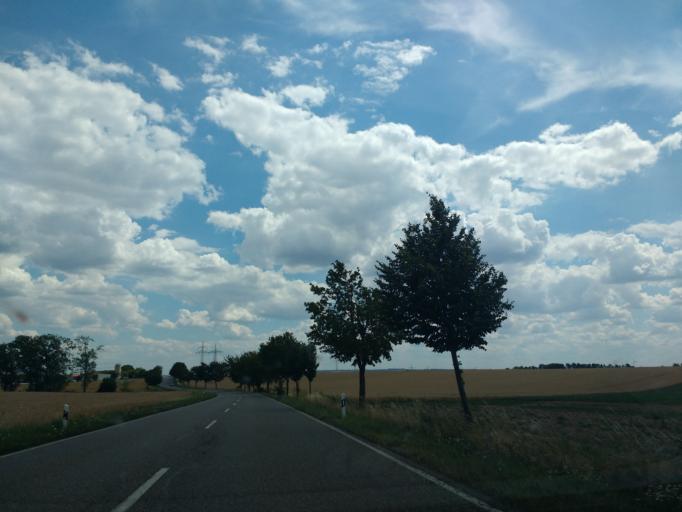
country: DE
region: Saxony-Anhalt
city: Droyssig
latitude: 51.0745
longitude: 12.0148
